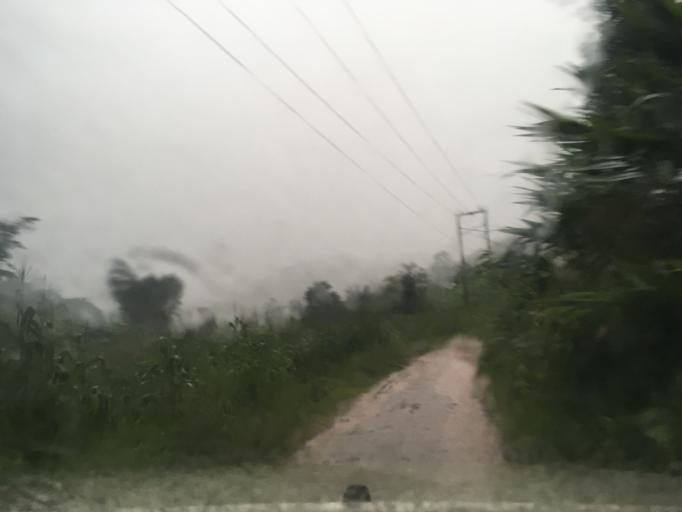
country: LA
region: Oudomxai
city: Muang La
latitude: 21.2358
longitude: 101.9571
